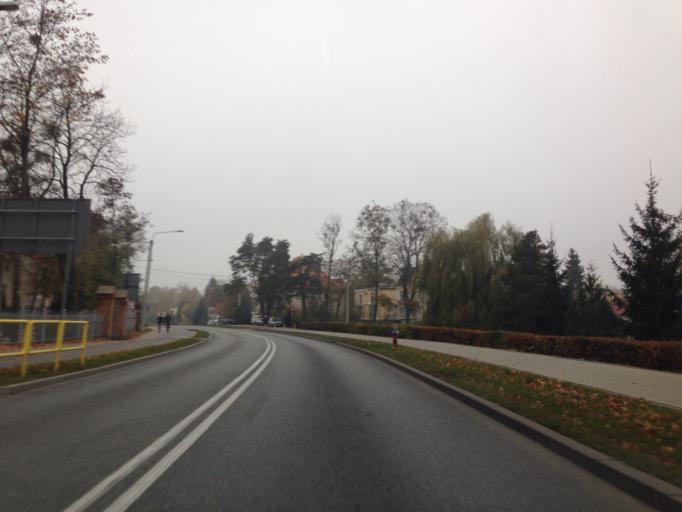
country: PL
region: Warmian-Masurian Voivodeship
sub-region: Powiat ilawski
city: Ilawa
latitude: 53.5979
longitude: 19.5535
